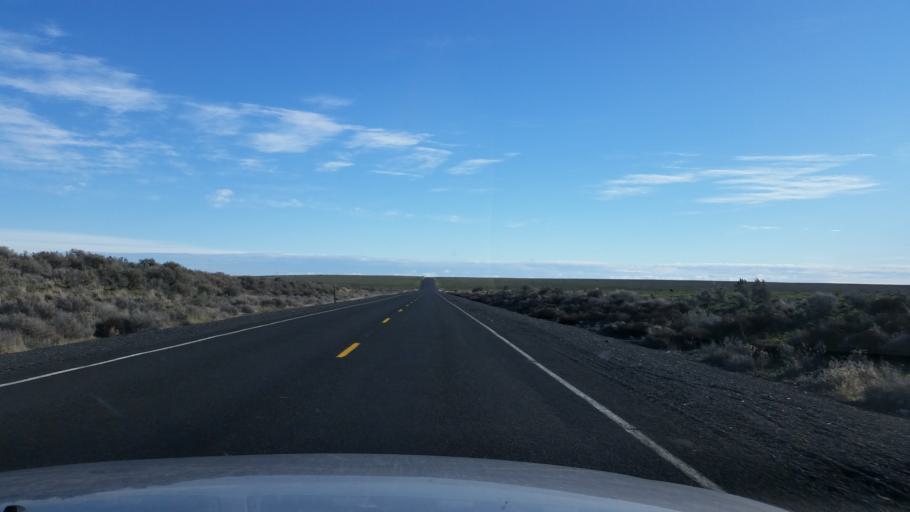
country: US
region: Washington
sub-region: Grant County
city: Moses Lake
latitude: 47.3572
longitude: -118.9548
